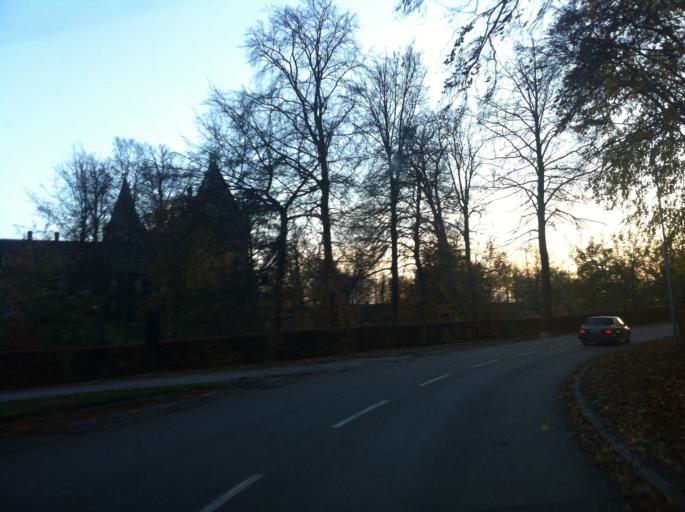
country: SE
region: Skane
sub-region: Eslovs Kommun
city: Eslov
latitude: 55.8713
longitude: 13.2441
